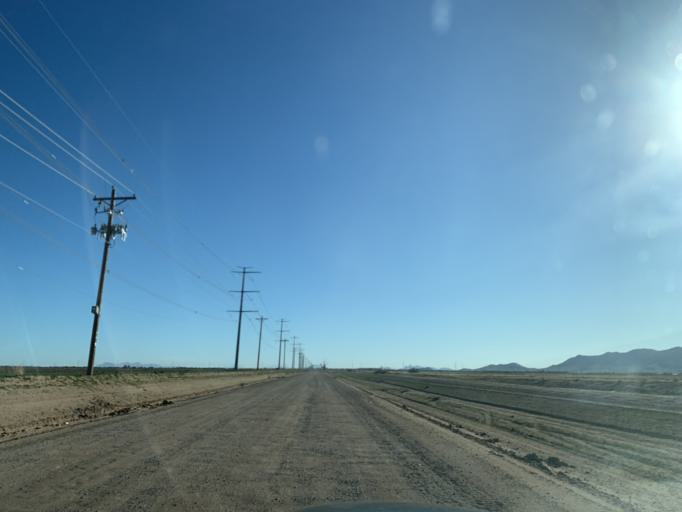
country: US
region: Arizona
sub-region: Pinal County
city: Casa Grande
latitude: 32.8598
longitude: -111.6709
